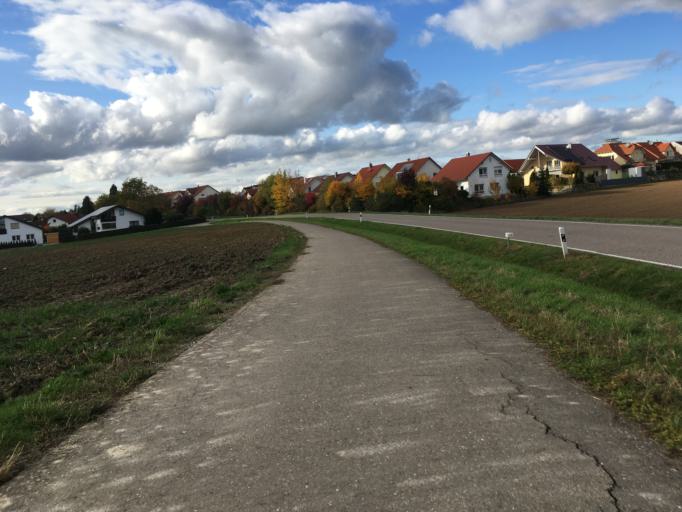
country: DE
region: Baden-Wuerttemberg
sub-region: Regierungsbezirk Stuttgart
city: Kuenzelsau
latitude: 49.2569
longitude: 9.6954
